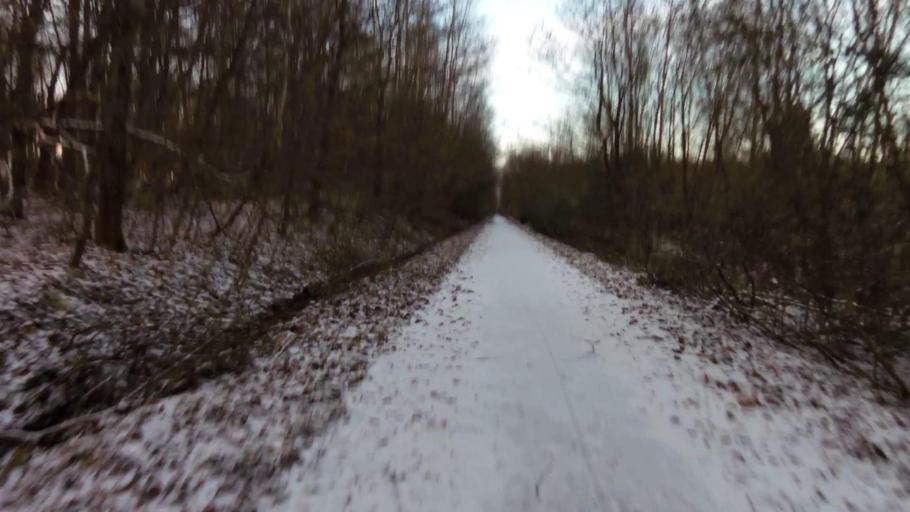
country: PL
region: West Pomeranian Voivodeship
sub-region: Powiat swidwinski
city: Polczyn-Zdroj
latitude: 53.7003
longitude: 16.0375
